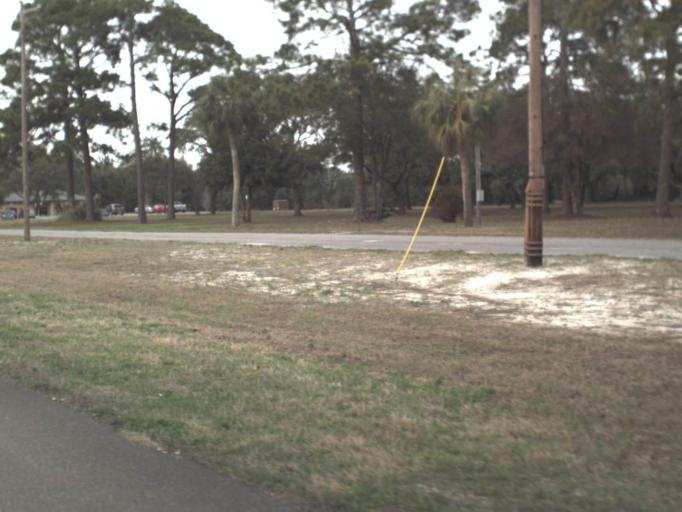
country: US
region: Florida
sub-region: Bay County
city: Tyndall Air Force Base
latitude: 30.0872
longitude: -85.6096
